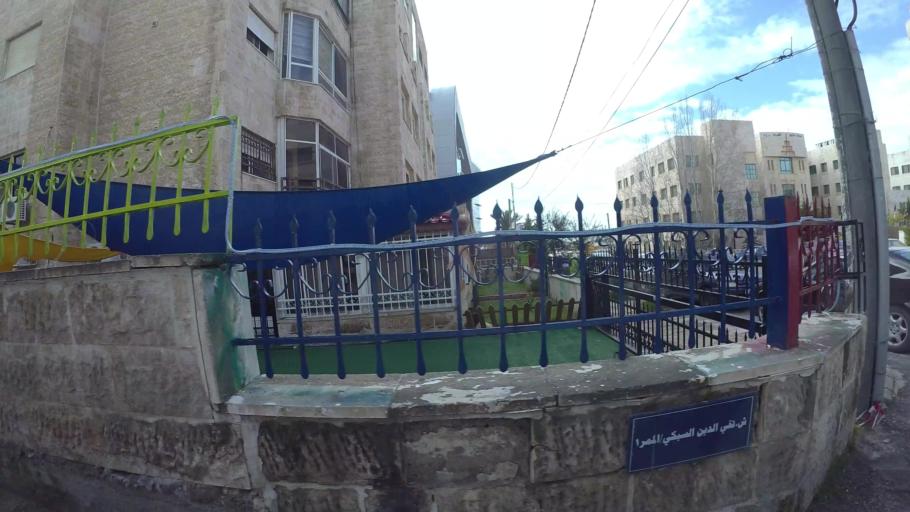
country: JO
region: Amman
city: Al Jubayhah
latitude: 31.9979
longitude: 35.8409
